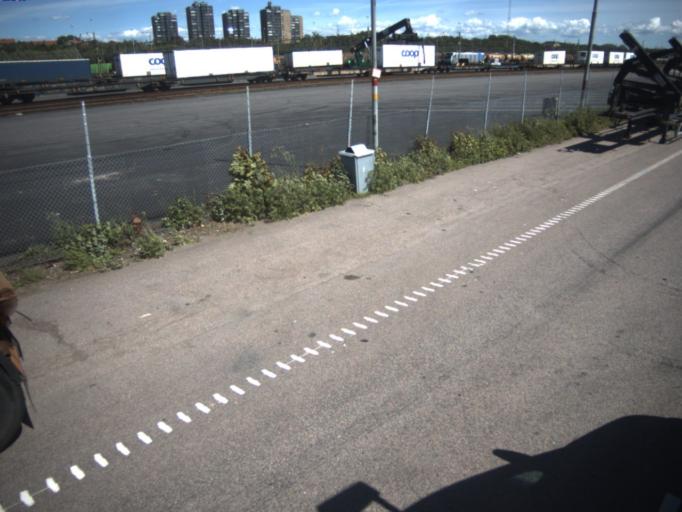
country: SE
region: Skane
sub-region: Helsingborg
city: Helsingborg
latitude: 56.0273
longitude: 12.7155
